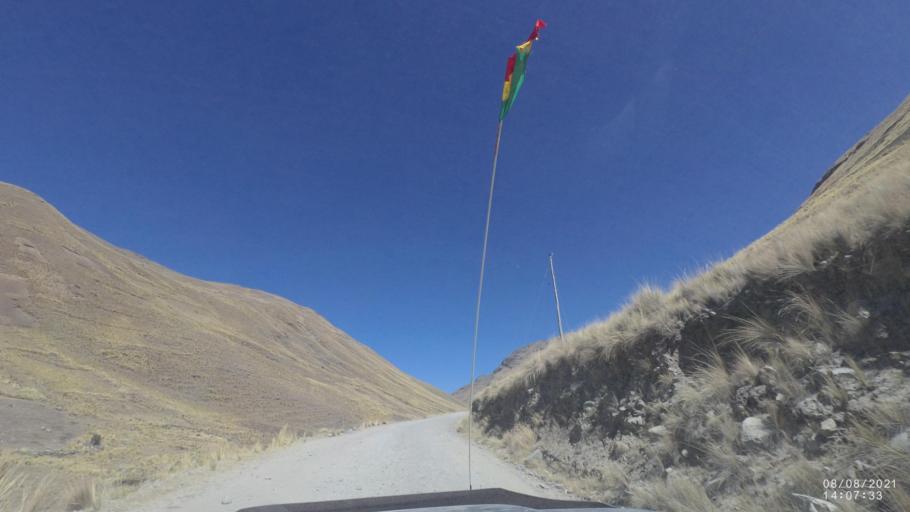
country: BO
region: Cochabamba
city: Sipe Sipe
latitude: -17.1306
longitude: -66.4398
